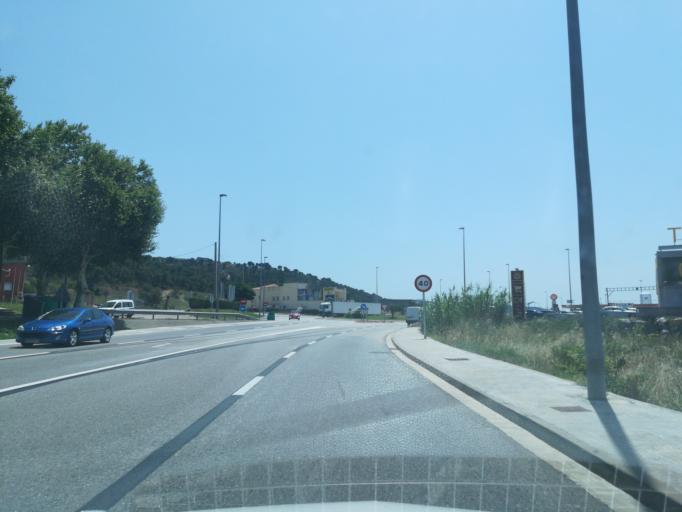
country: ES
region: Catalonia
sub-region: Provincia de Girona
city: la Jonquera
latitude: 42.4121
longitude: 2.8755
